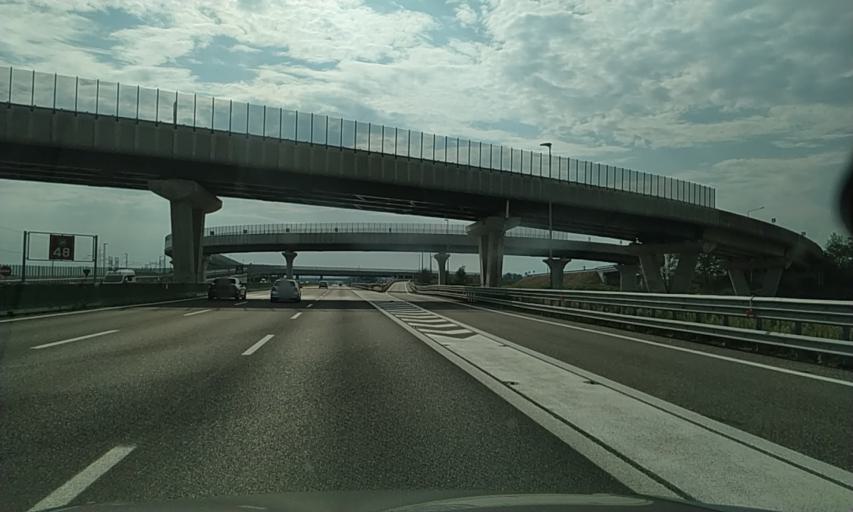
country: IT
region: Piedmont
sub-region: Provincia di Vercelli
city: Formigliana
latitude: 45.4500
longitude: 8.3040
